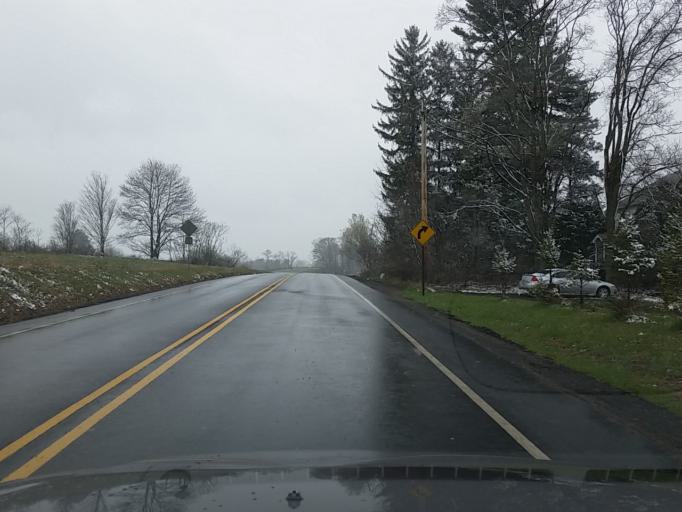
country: US
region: Pennsylvania
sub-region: Columbia County
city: Mifflinville
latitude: 41.1964
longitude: -76.3331
